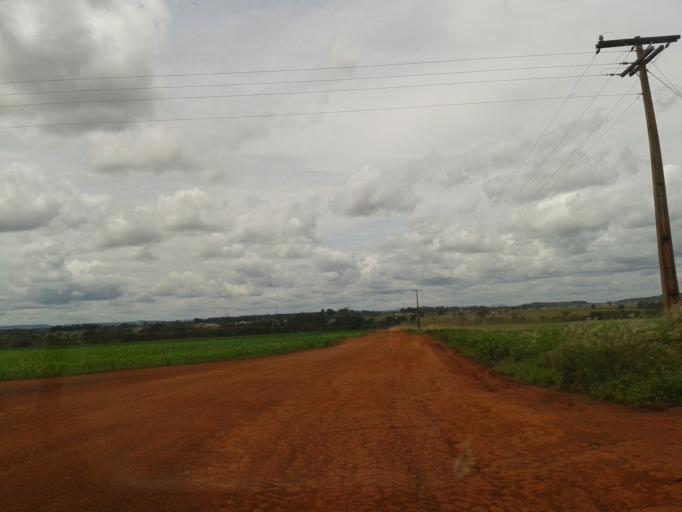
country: BR
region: Minas Gerais
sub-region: Centralina
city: Centralina
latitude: -18.5929
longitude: -49.2216
